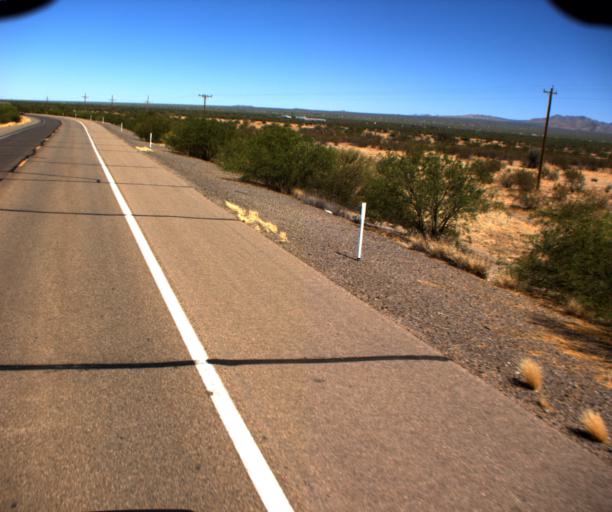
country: US
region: Arizona
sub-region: Pima County
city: Three Points
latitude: 32.0753
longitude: -111.3365
